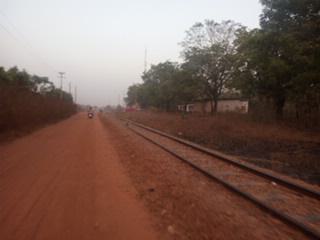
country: BJ
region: Borgou
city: Parakou
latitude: 9.3398
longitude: 2.6054
